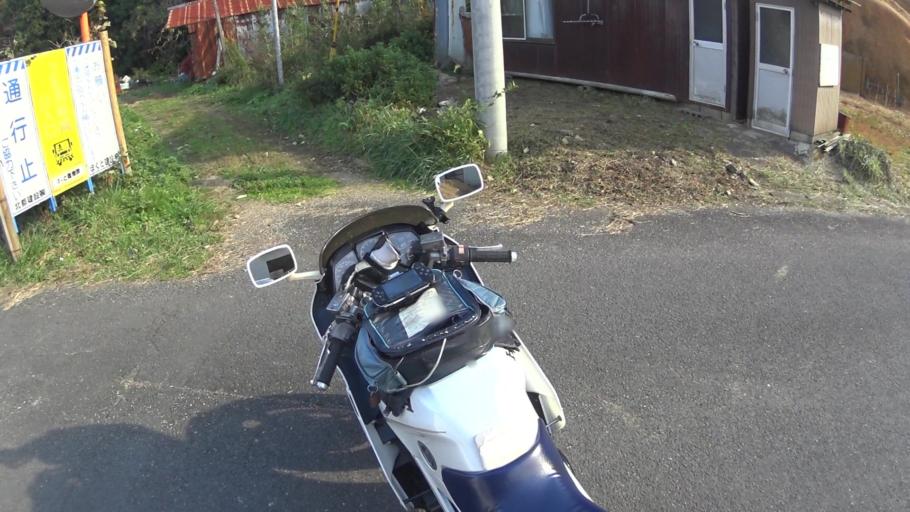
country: JP
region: Kyoto
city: Maizuru
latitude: 35.5594
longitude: 135.4039
